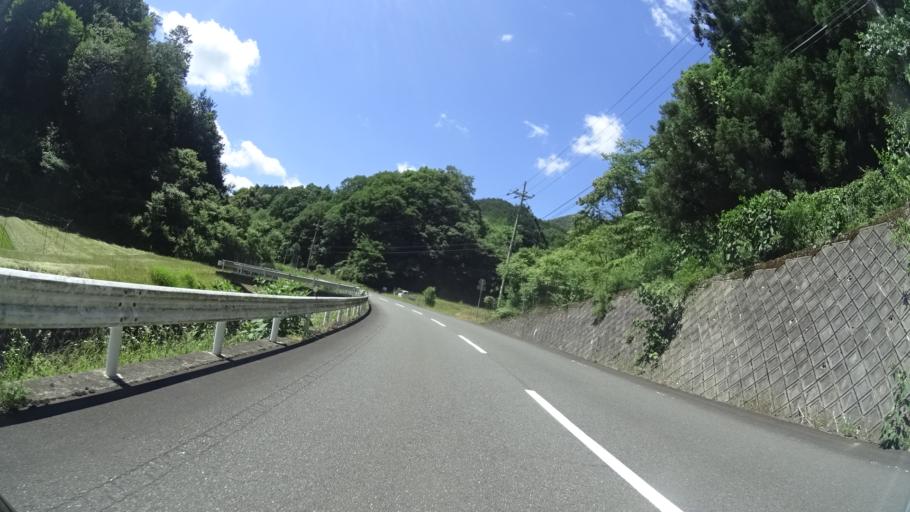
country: JP
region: Kyoto
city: Miyazu
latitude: 35.4183
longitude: 135.1859
